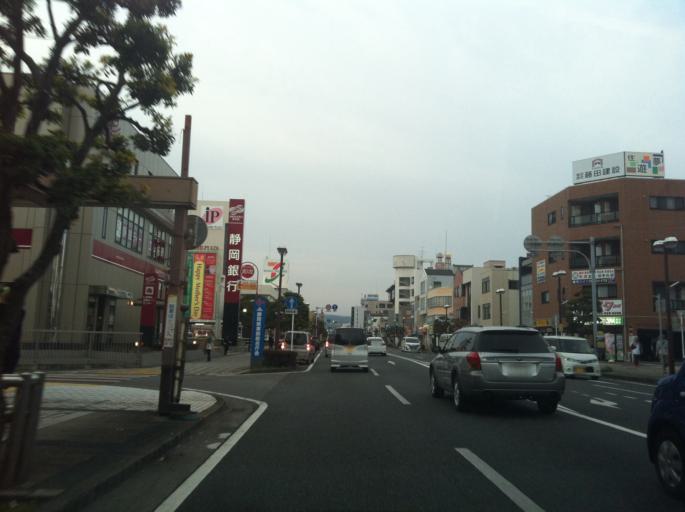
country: JP
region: Shizuoka
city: Numazu
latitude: 35.1062
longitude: 138.8584
